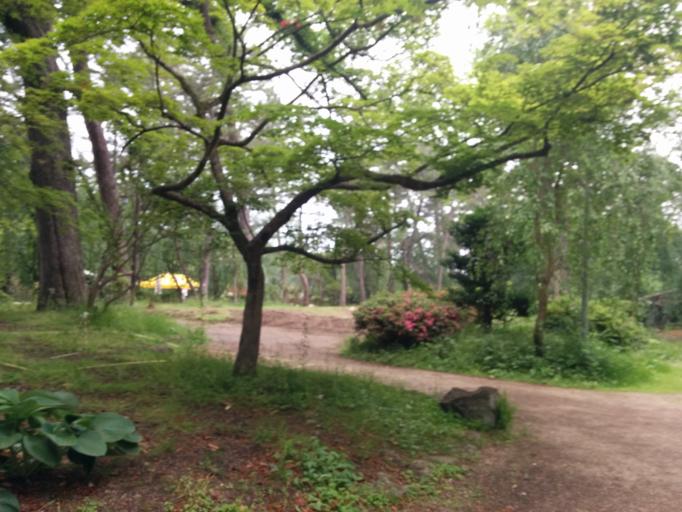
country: JP
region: Aomori
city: Hirosaki
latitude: 40.6062
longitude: 140.4649
